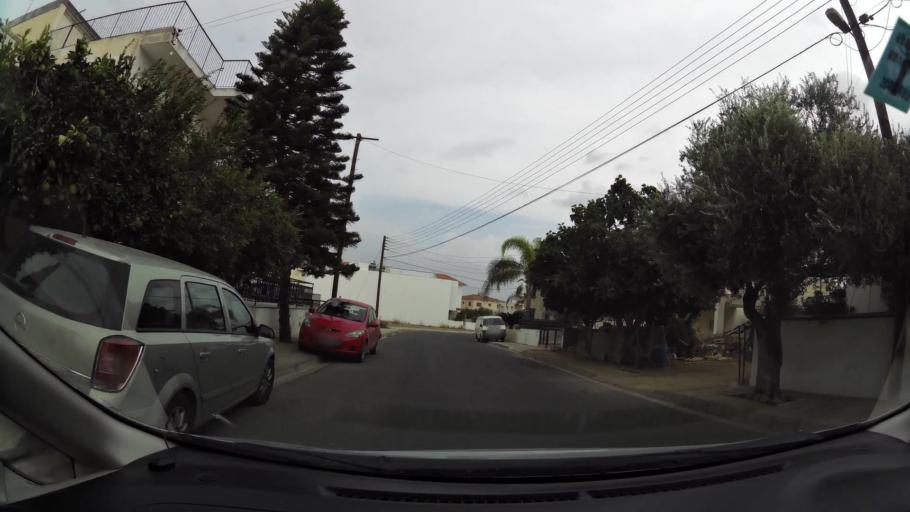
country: CY
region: Lefkosia
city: Geri
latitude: 35.1036
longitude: 33.3912
